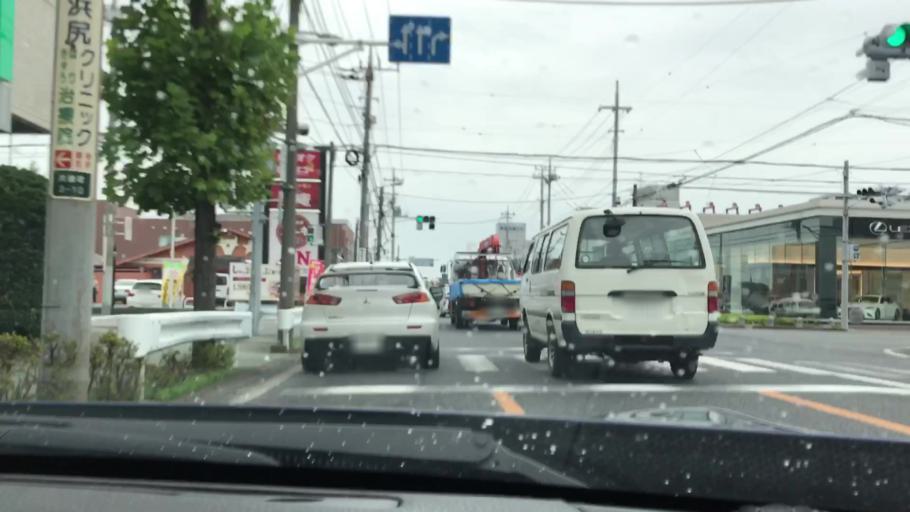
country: JP
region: Gunma
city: Takasaki
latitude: 36.3490
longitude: 139.0148
